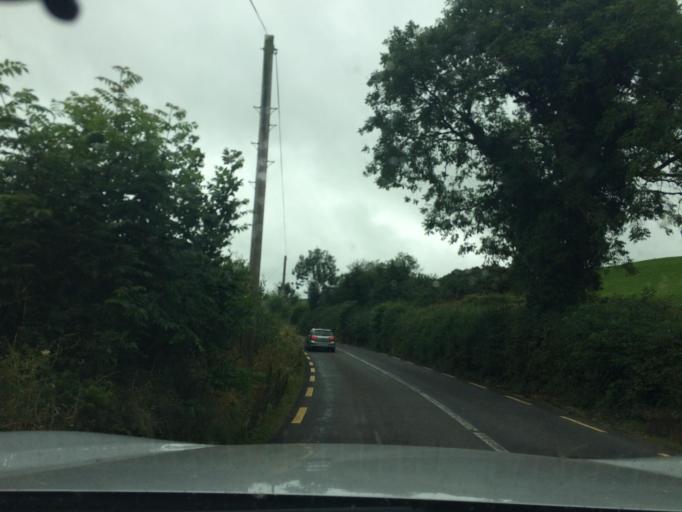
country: IE
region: Munster
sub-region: South Tipperary
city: Cluain Meala
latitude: 52.2472
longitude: -7.7187
